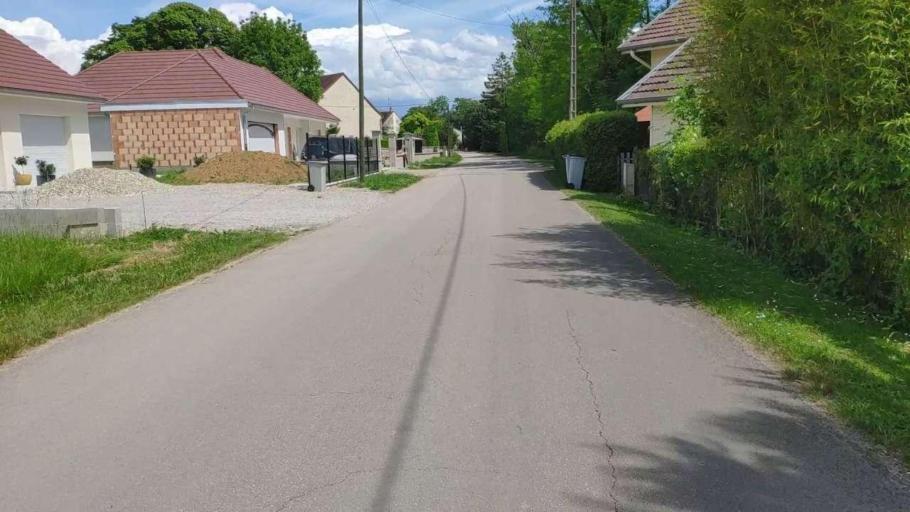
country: FR
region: Franche-Comte
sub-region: Departement du Jura
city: Bletterans
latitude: 46.7447
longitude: 5.4876
